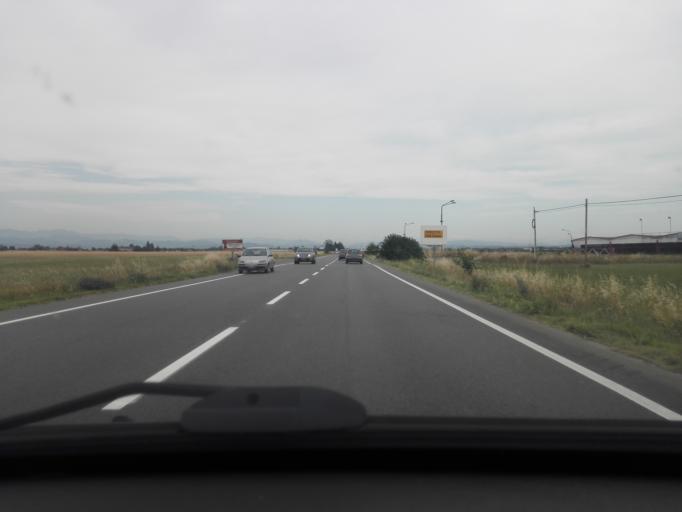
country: IT
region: Piedmont
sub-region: Provincia di Alessandria
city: Pozzolo Formigaro
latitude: 44.8193
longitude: 8.7543
